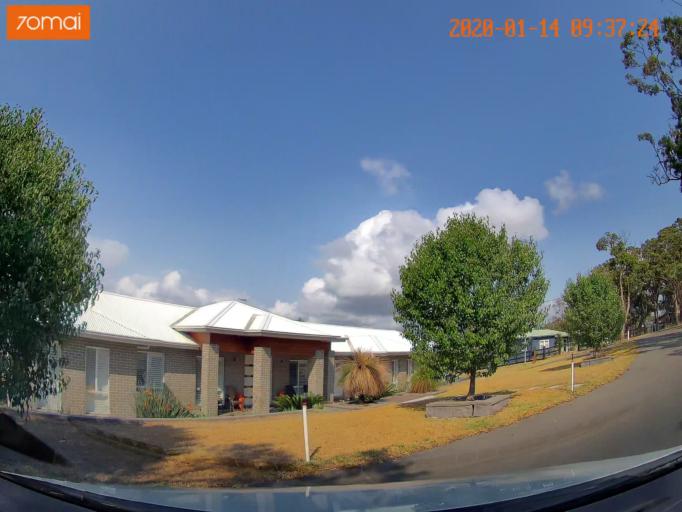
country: AU
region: New South Wales
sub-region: Wyong Shire
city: Kingfisher Shores
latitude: -33.1164
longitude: 151.5599
